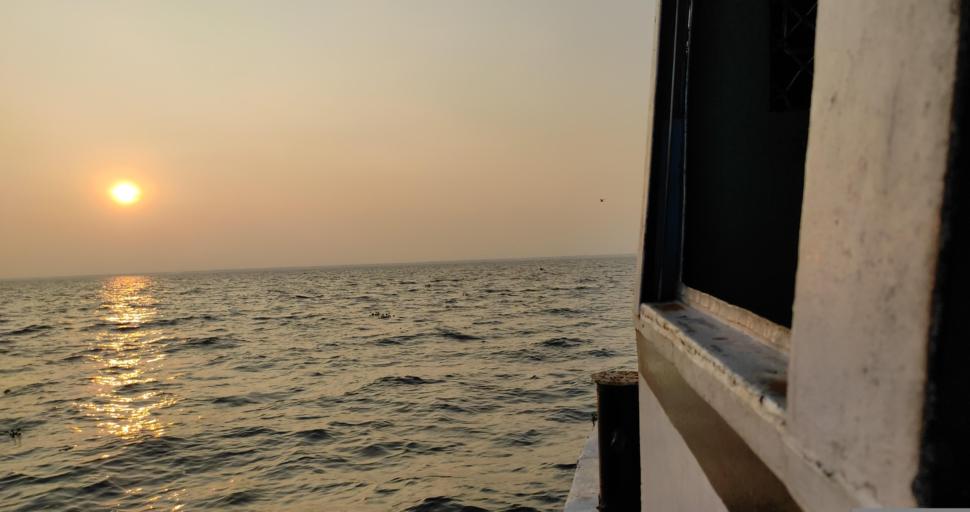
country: IN
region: Kerala
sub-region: Kottayam
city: Kottayam
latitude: 9.5985
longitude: 76.4222
